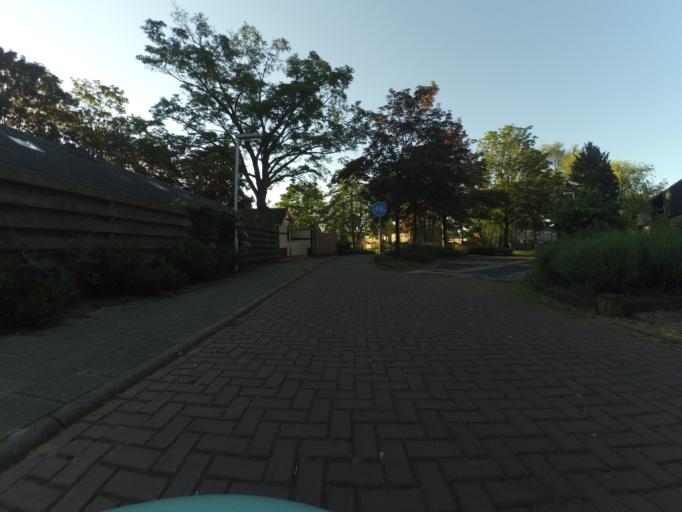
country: NL
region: Gelderland
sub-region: Gemeente Barneveld
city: Barneveld
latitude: 52.1337
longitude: 5.5772
